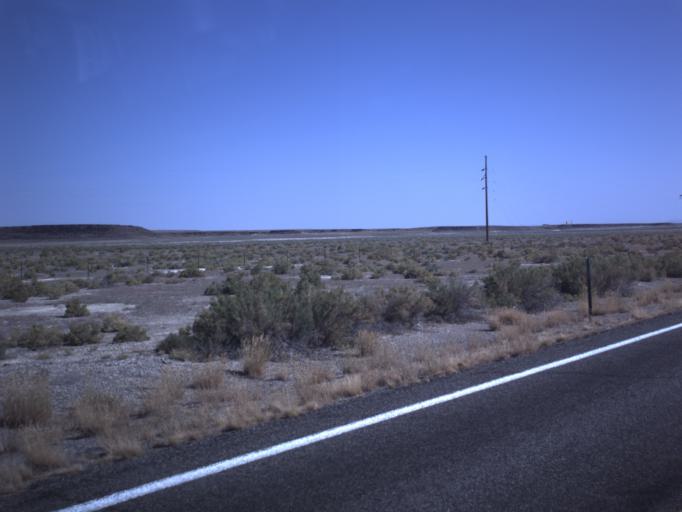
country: US
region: Utah
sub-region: Millard County
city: Delta
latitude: 39.1588
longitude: -112.7137
